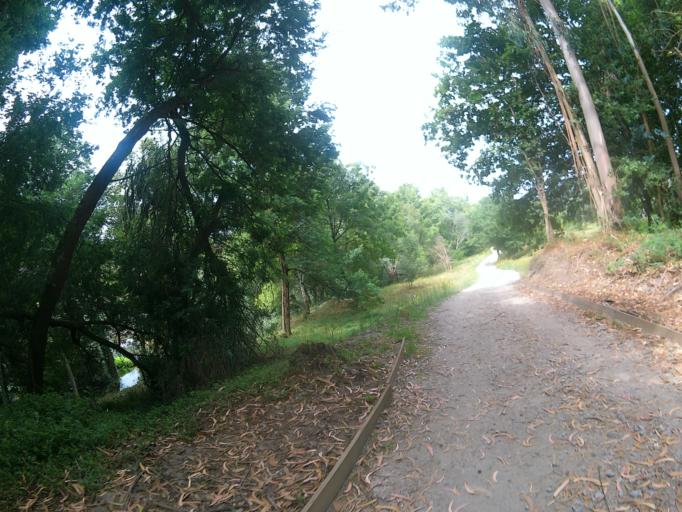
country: PT
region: Viana do Castelo
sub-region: Ponte de Lima
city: Ponte de Lima
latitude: 41.7841
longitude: -8.5262
